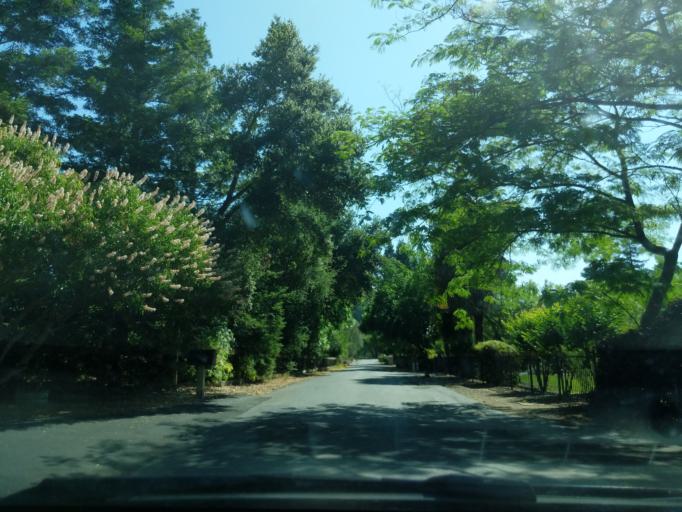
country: US
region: California
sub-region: Santa Clara County
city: Morgan Hill
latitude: 37.1018
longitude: -121.6754
